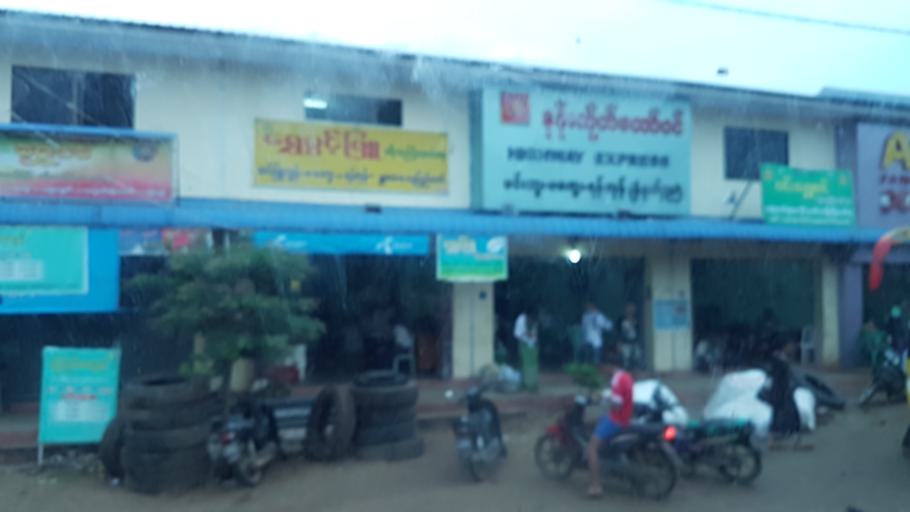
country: MM
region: Magway
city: Magway
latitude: 20.1540
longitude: 94.9420
